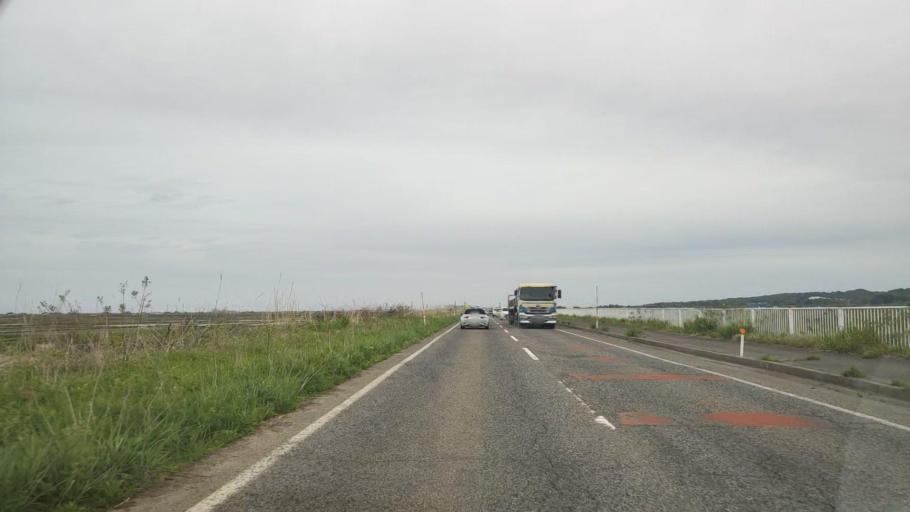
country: JP
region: Niigata
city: Niitsu-honcho
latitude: 37.7614
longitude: 139.0954
